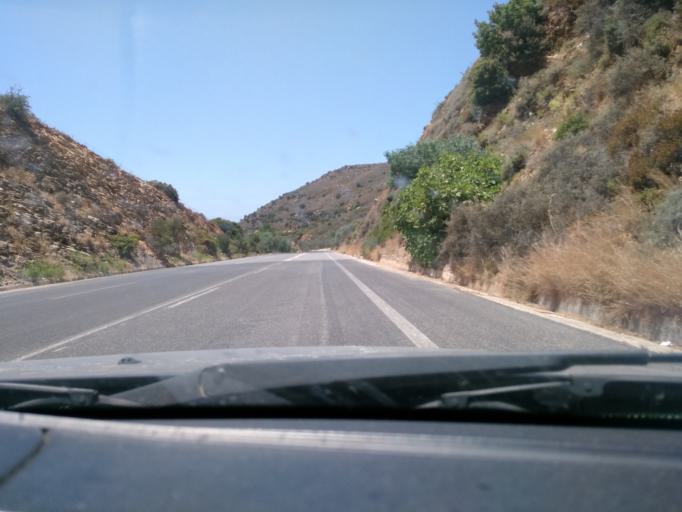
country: GR
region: Crete
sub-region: Nomos Rethymnis
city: Panormos
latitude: 35.4097
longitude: 24.7518
